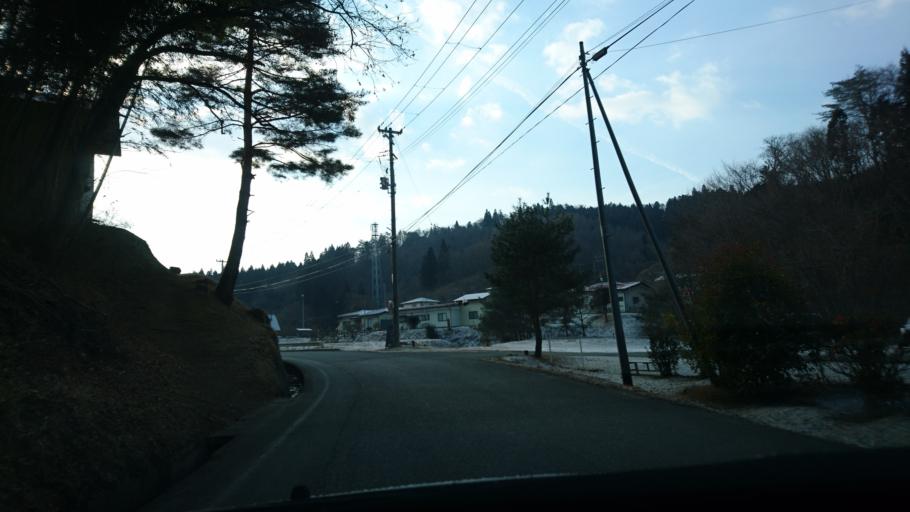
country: JP
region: Iwate
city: Ichinoseki
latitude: 38.9175
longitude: 141.3593
